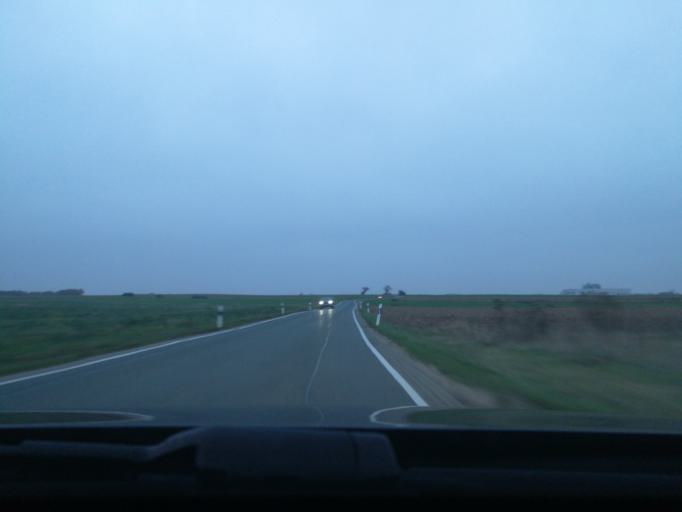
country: DE
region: Bavaria
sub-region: Regierungsbezirk Mittelfranken
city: Obermichelbach
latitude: 49.4933
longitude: 10.9279
